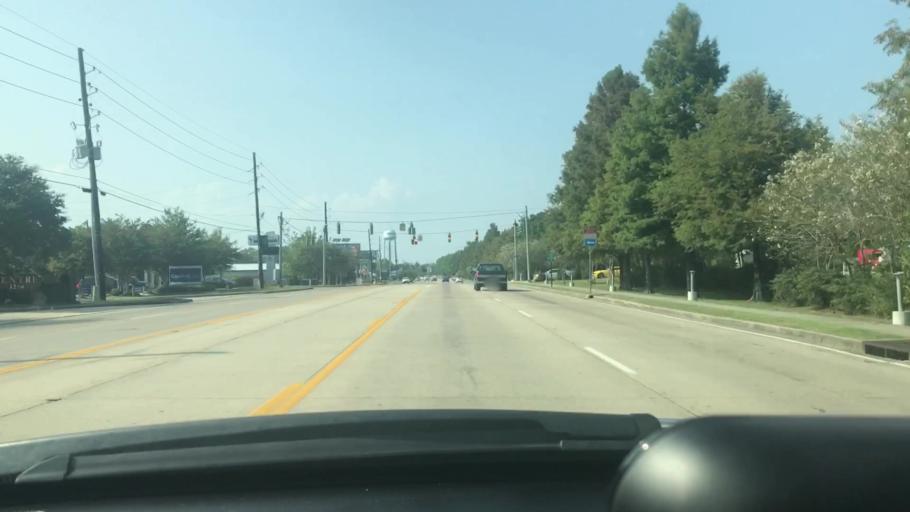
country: US
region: Louisiana
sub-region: Tangipahoa Parish
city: Hammond
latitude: 30.4928
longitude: -90.4579
